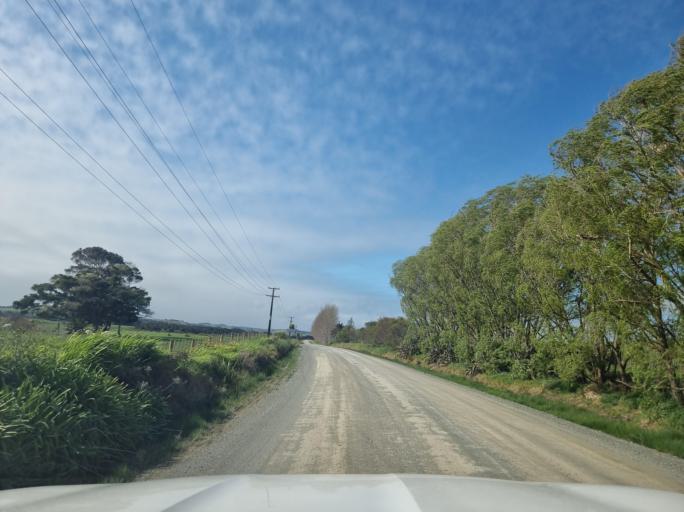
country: NZ
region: Auckland
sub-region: Auckland
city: Wellsford
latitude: -36.1150
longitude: 174.5001
